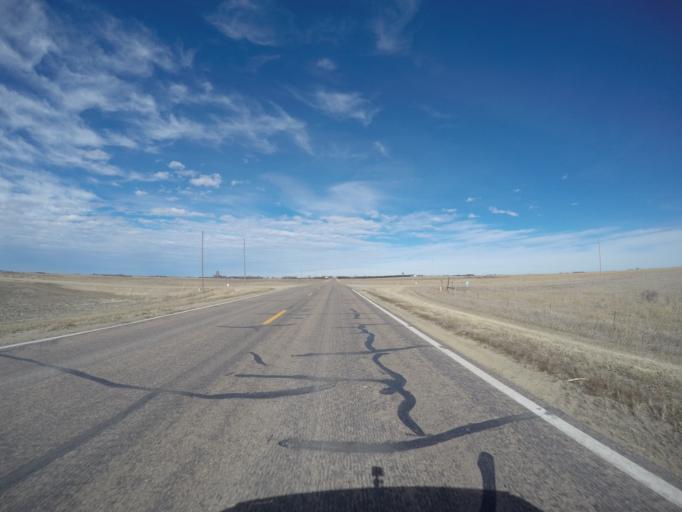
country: US
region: Nebraska
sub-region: Franklin County
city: Franklin
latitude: 40.1899
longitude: -98.9525
